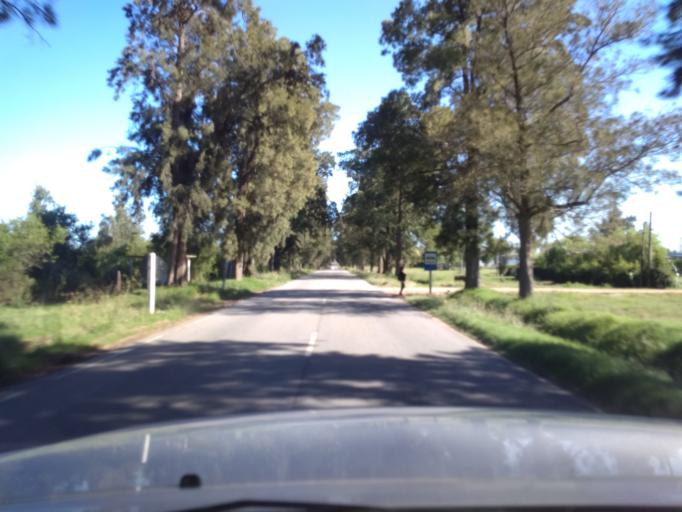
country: UY
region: Canelones
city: San Bautista
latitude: -34.3769
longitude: -55.9595
